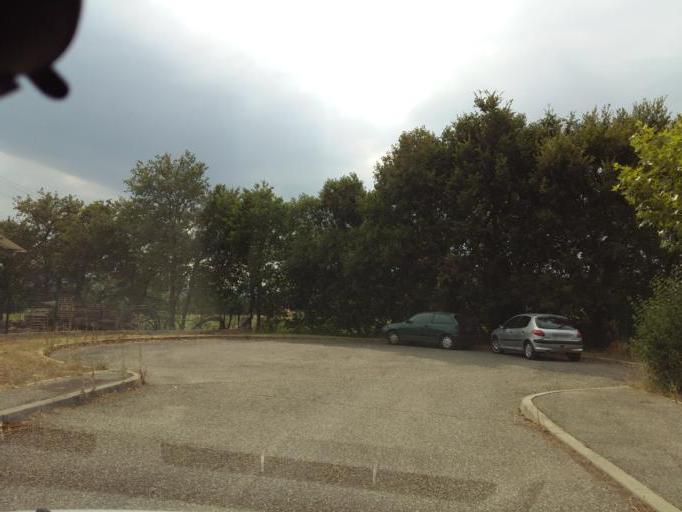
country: FR
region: Provence-Alpes-Cote d'Azur
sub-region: Departement du Vaucluse
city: Roussillon
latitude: 43.8653
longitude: 5.2894
